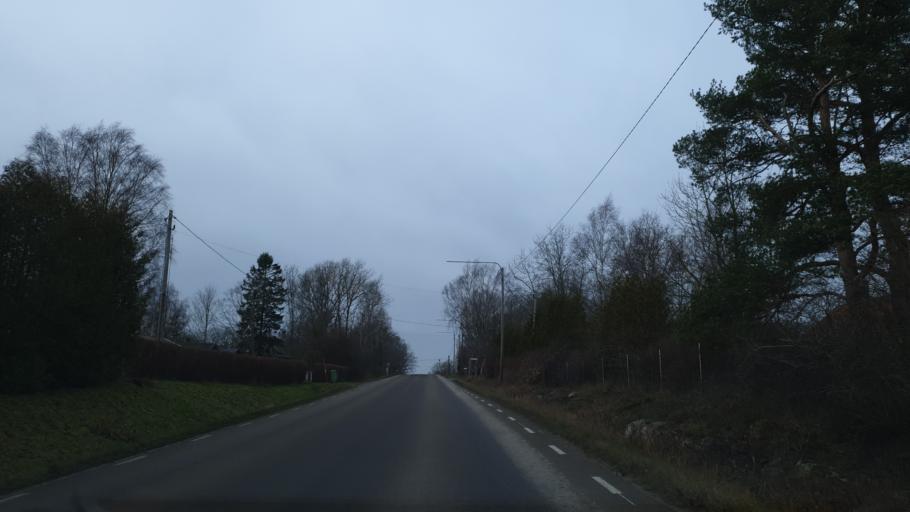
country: SE
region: Blekinge
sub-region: Karlskrona Kommun
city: Sturko
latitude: 56.1118
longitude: 15.7050
